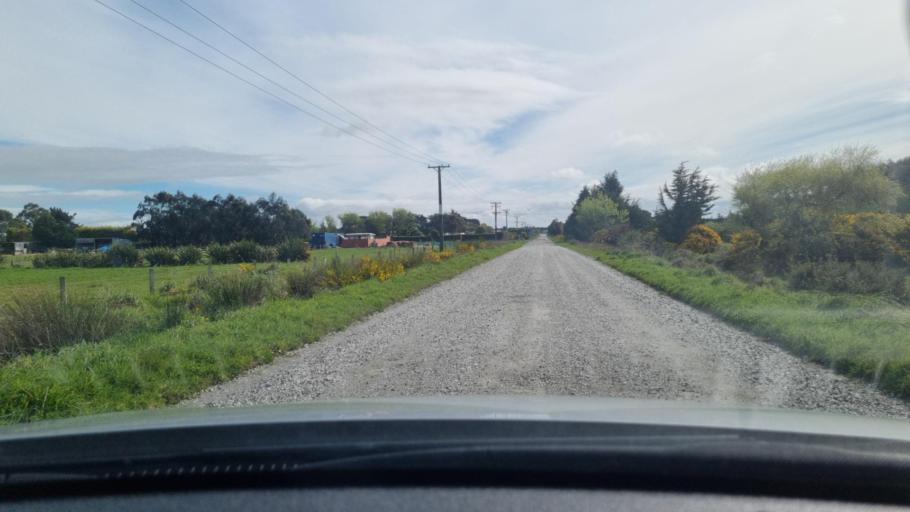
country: NZ
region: Southland
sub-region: Invercargill City
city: Invercargill
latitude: -46.4506
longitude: 168.3907
